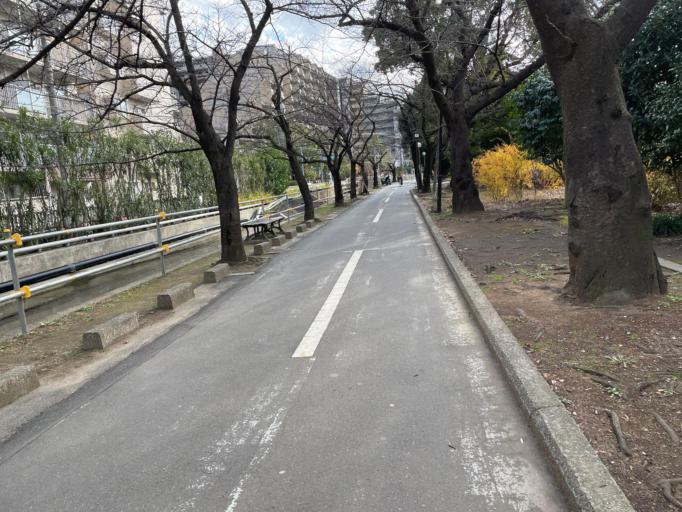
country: JP
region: Tokyo
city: Urayasu
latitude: 35.6812
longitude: 139.8389
